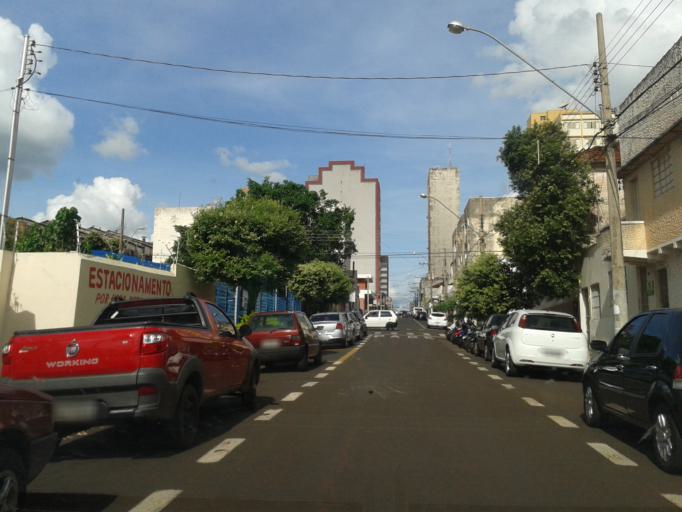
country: BR
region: Minas Gerais
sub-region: Ituiutaba
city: Ituiutaba
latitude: -18.9744
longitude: -49.4650
